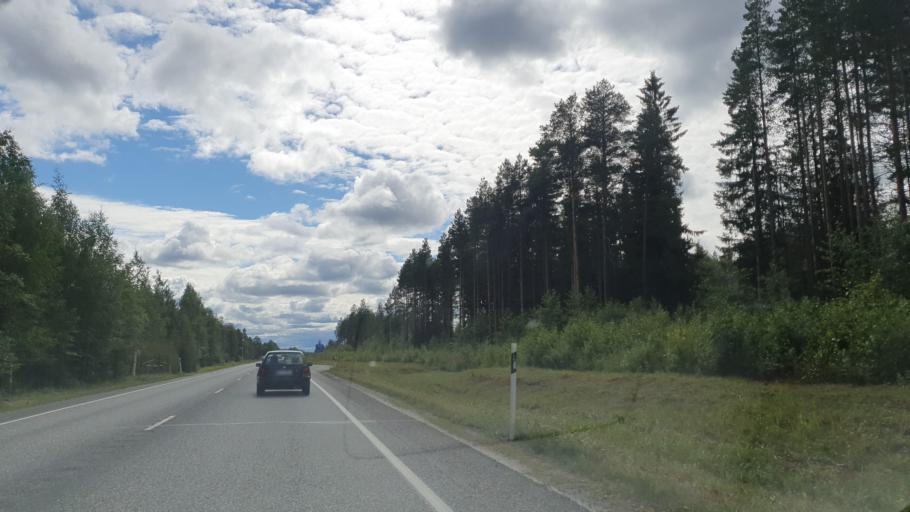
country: FI
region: Kainuu
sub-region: Kajaani
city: Kajaani
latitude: 64.1643
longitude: 27.5259
